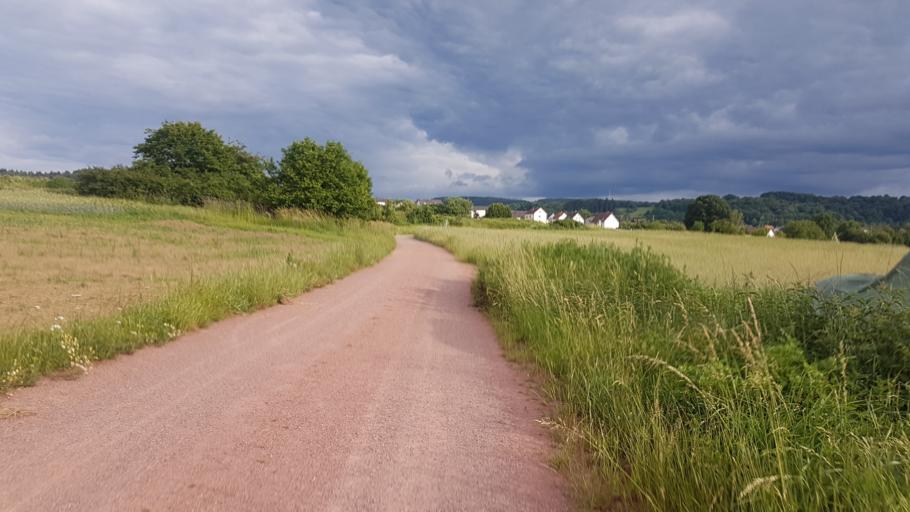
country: DE
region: Saarland
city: Britten
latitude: 49.4870
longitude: 6.7023
